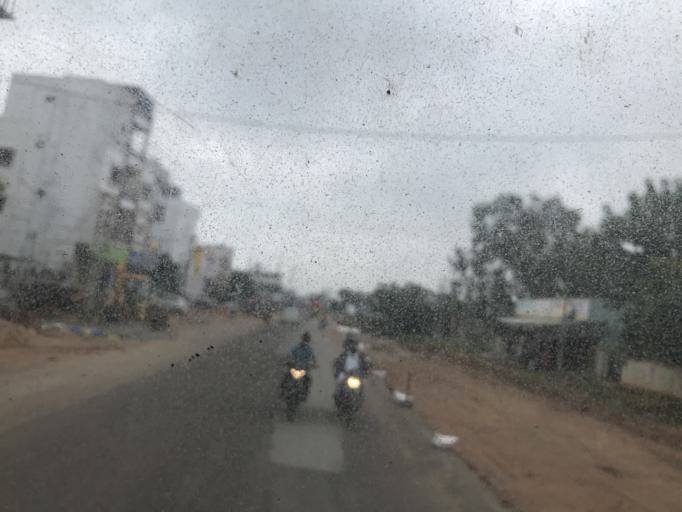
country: IN
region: Telangana
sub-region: Mahbubnagar
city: Mahbubnagar
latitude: 16.7740
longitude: 78.1269
